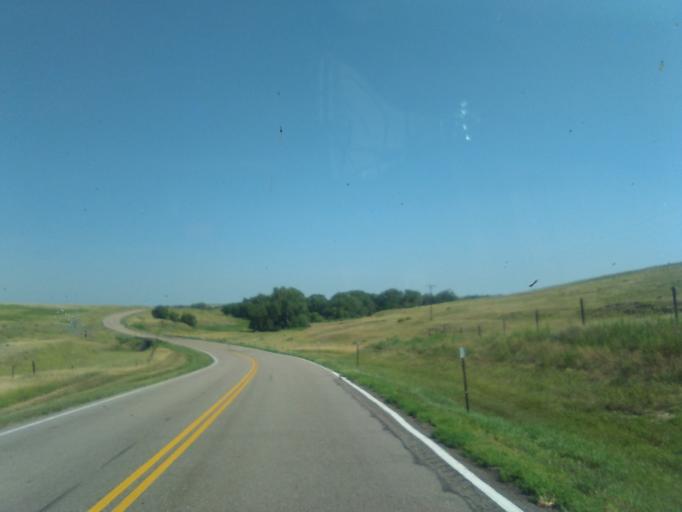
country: US
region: Nebraska
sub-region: Dundy County
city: Benkelman
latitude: 39.8850
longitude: -101.5411
